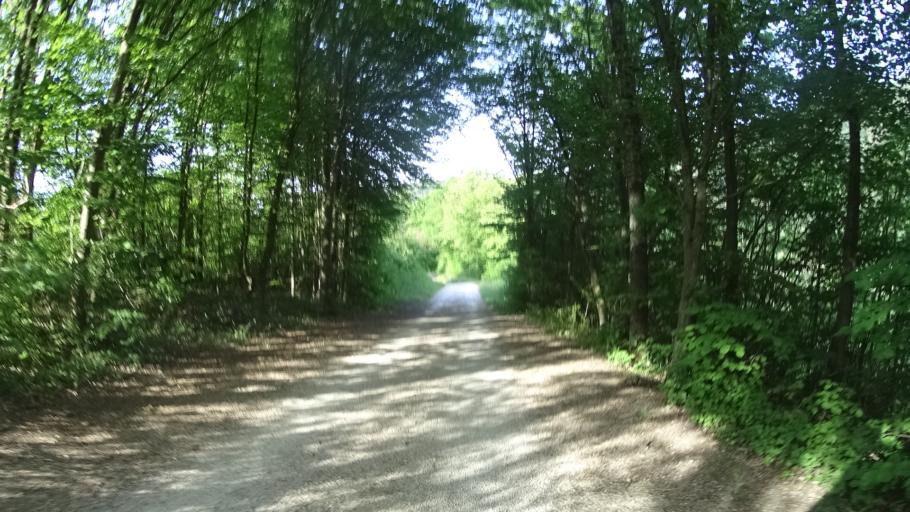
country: DE
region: Bavaria
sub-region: Lower Bavaria
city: Riedenburg
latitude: 48.9717
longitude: 11.6857
